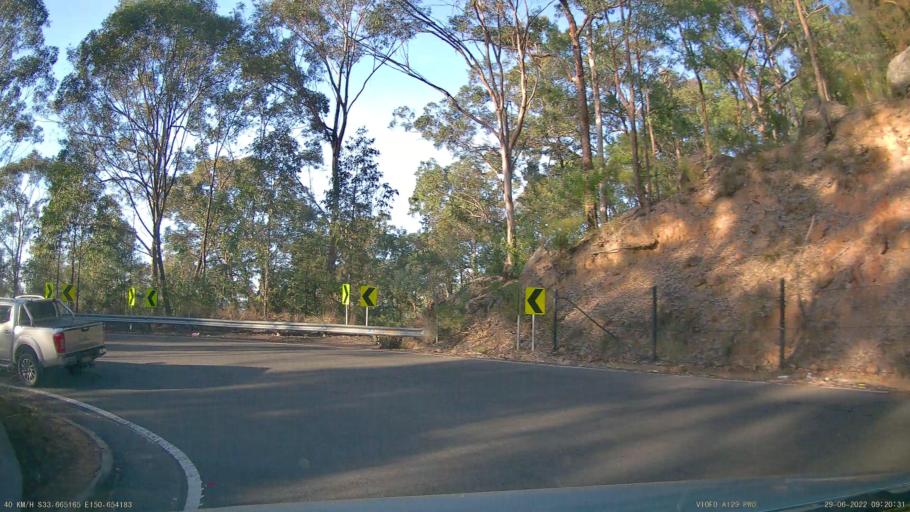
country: AU
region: New South Wales
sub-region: Penrith Municipality
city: Emu Heights
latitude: -33.6653
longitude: 150.6542
